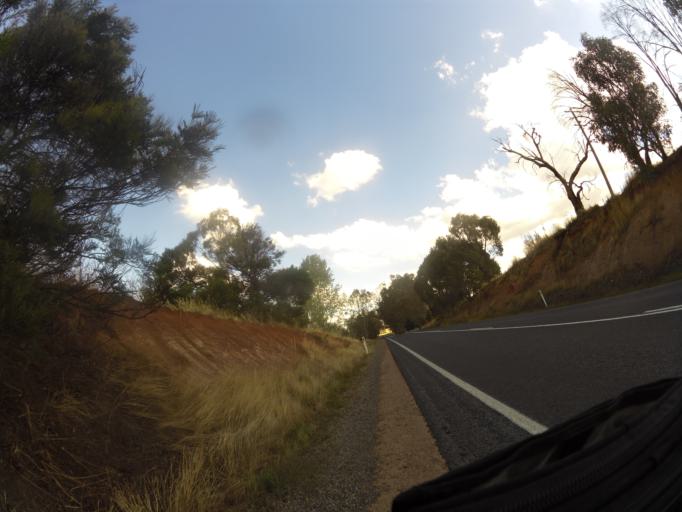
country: AU
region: Victoria
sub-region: Mansfield
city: Mansfield
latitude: -36.9372
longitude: 145.9992
